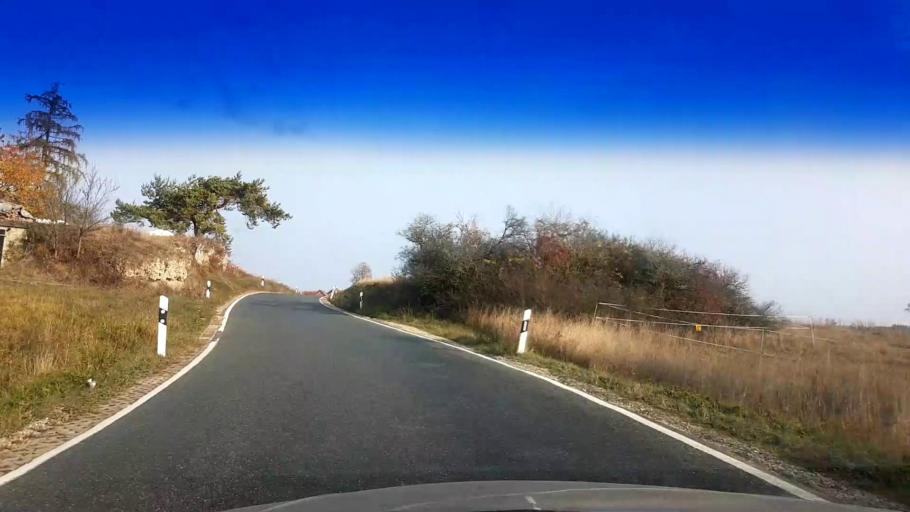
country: DE
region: Bavaria
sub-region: Upper Franconia
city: Stadelhofen
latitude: 50.0148
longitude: 11.2007
